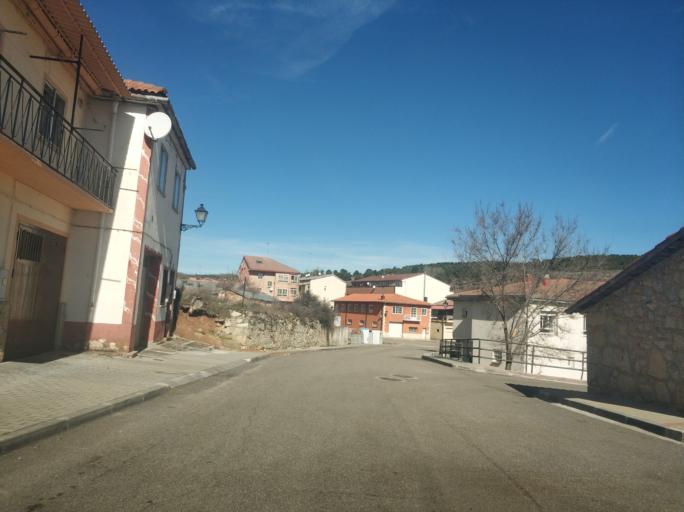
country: ES
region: Castille and Leon
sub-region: Provincia de Soria
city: San Leonardo de Yague
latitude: 41.8309
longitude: -3.0720
